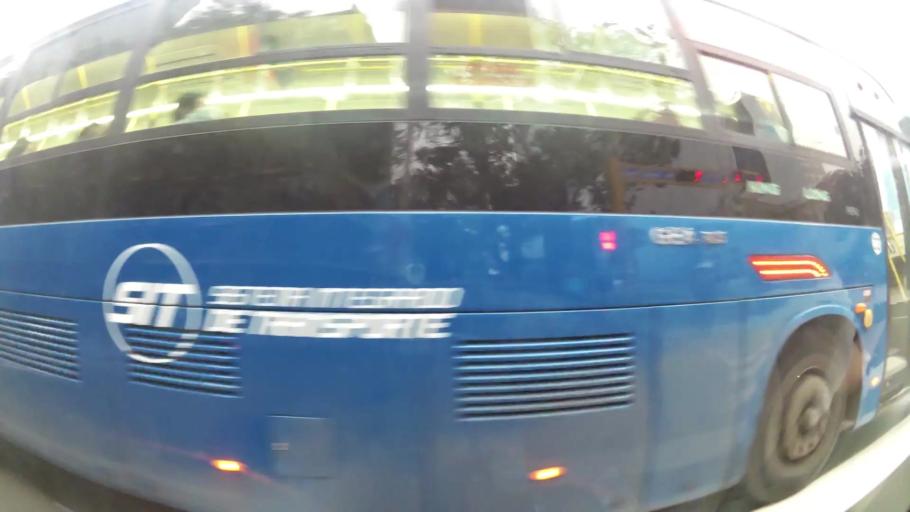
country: PE
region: Lima
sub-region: Lima
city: San Isidro
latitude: -12.0915
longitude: -77.0271
